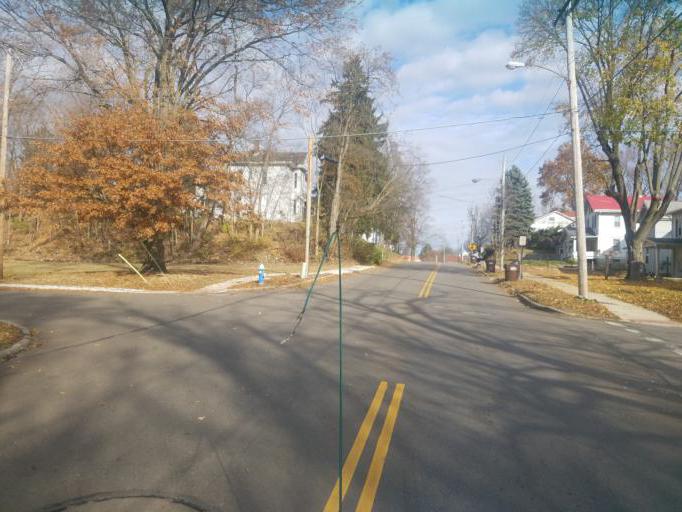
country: US
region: Ohio
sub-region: Richland County
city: Mansfield
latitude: 40.7517
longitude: -82.5230
